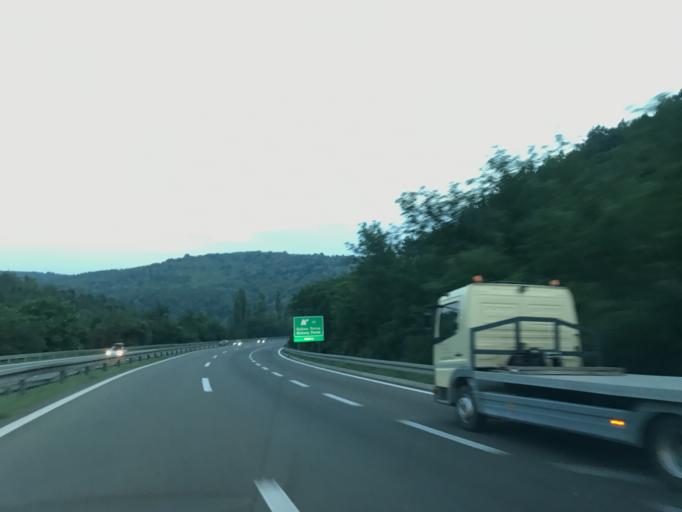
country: RS
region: Central Serbia
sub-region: Belgrade
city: Zvezdara
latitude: 44.7408
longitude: 20.5449
